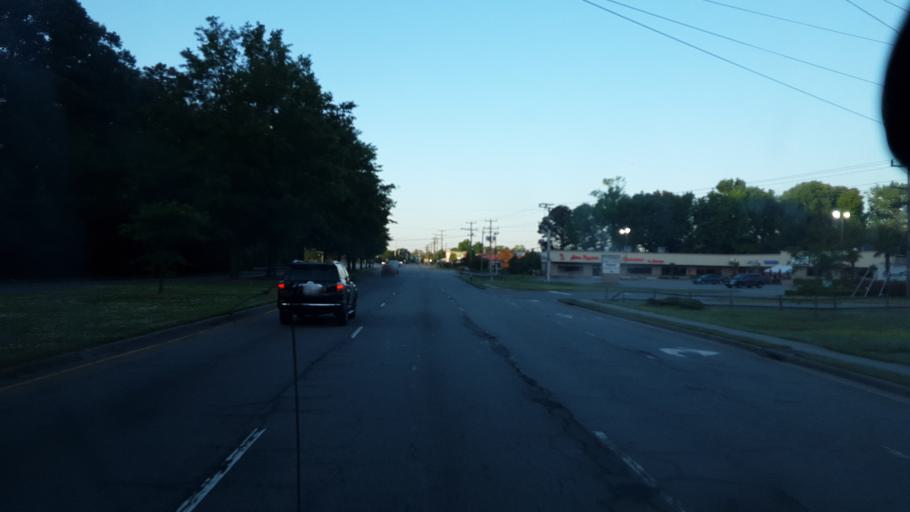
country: US
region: Virginia
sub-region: City of Virginia Beach
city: Virginia Beach
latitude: 36.7910
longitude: -75.9967
